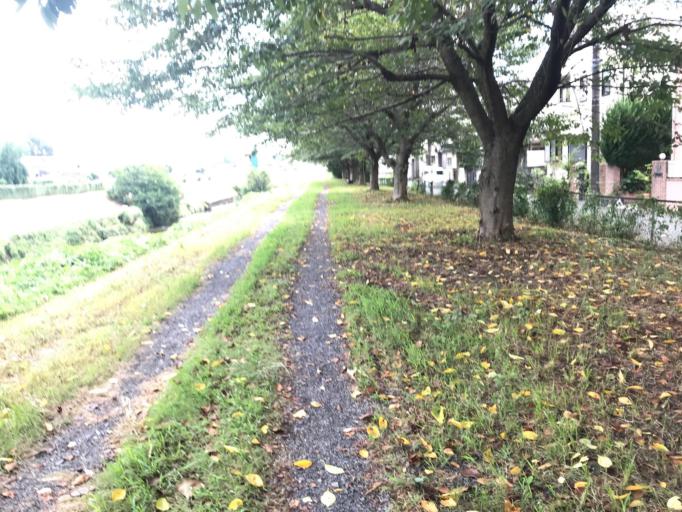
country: JP
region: Tokyo
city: Tanashicho
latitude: 35.7714
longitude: 139.5592
